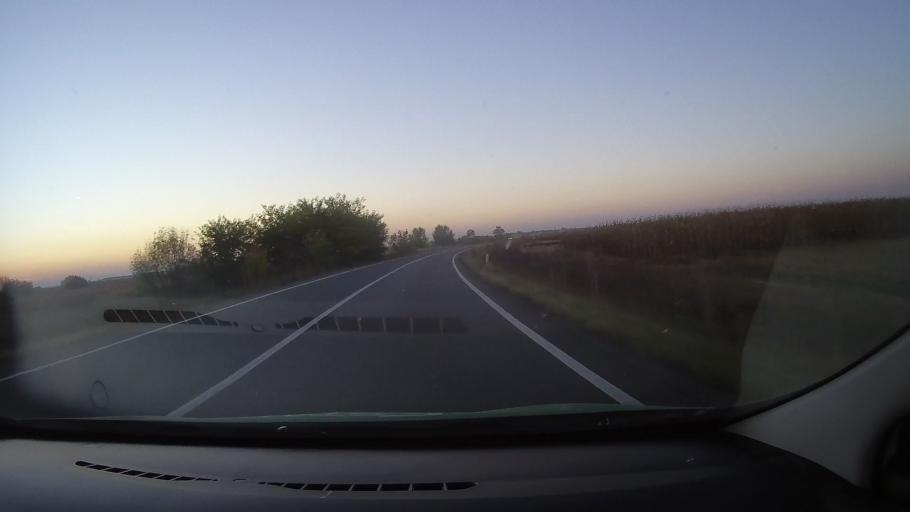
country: RO
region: Bihor
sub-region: Comuna Tarcea
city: Tarcea
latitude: 47.4398
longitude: 22.1936
